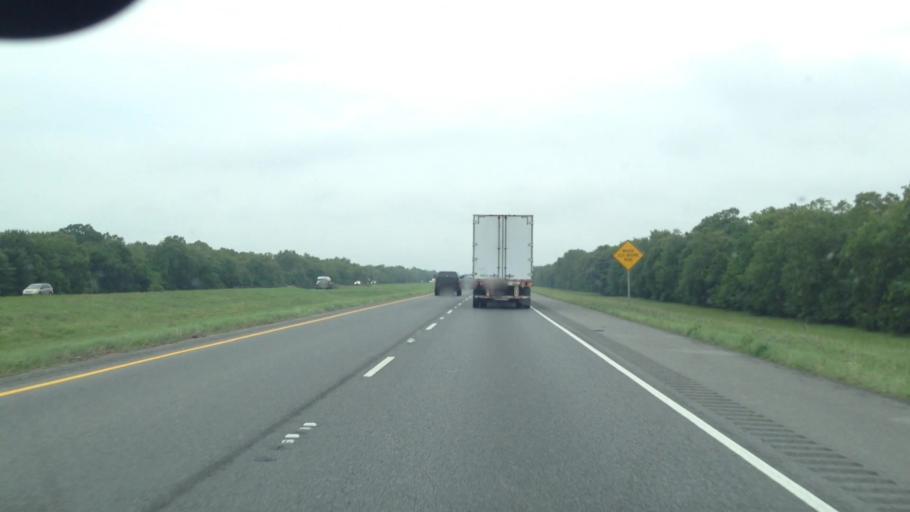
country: US
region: Louisiana
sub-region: Saint Landry Parish
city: Opelousas
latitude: 30.7029
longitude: -92.0907
